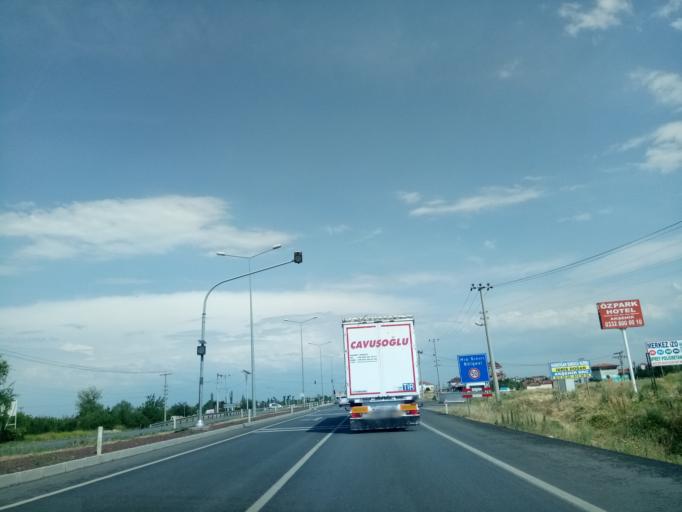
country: TR
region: Konya
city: Aksehir
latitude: 38.3792
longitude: 31.4210
